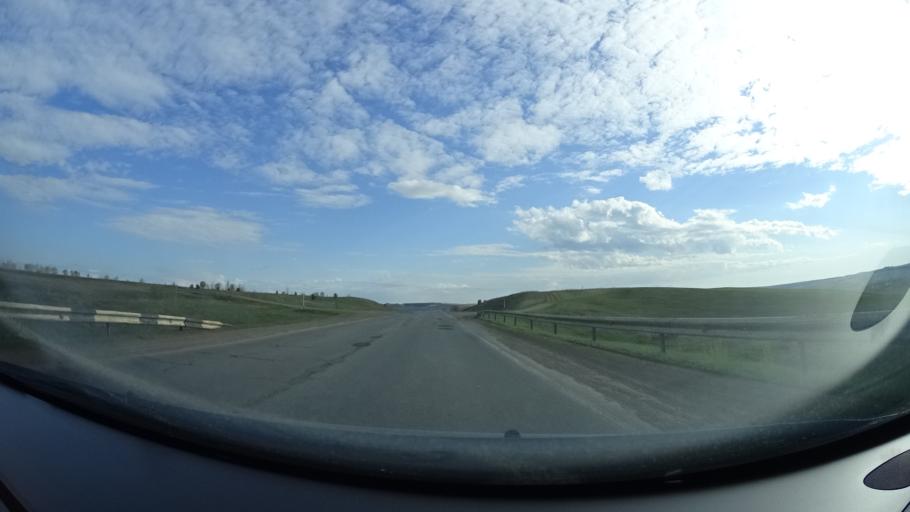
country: RU
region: Bashkortostan
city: Blagoveshchensk
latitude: 55.0948
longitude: 55.8156
